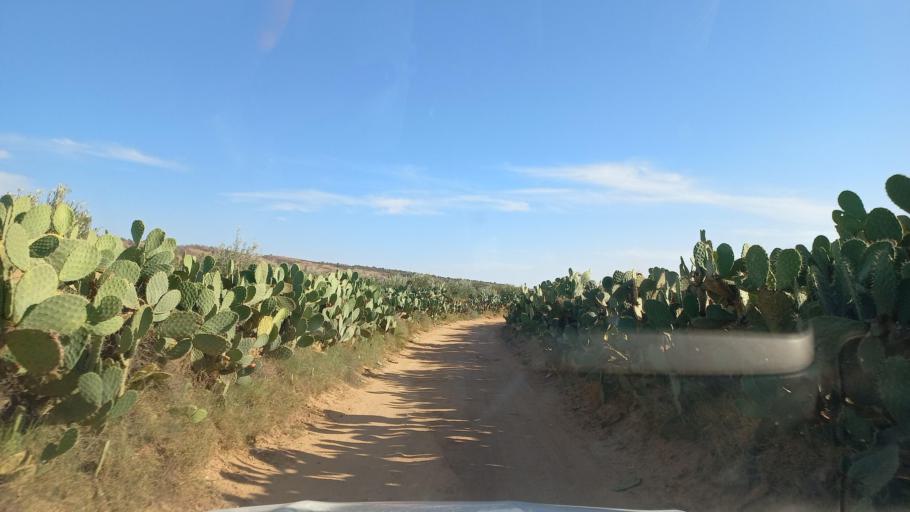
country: TN
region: Al Qasrayn
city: Sbiba
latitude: 35.3340
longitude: 9.1253
